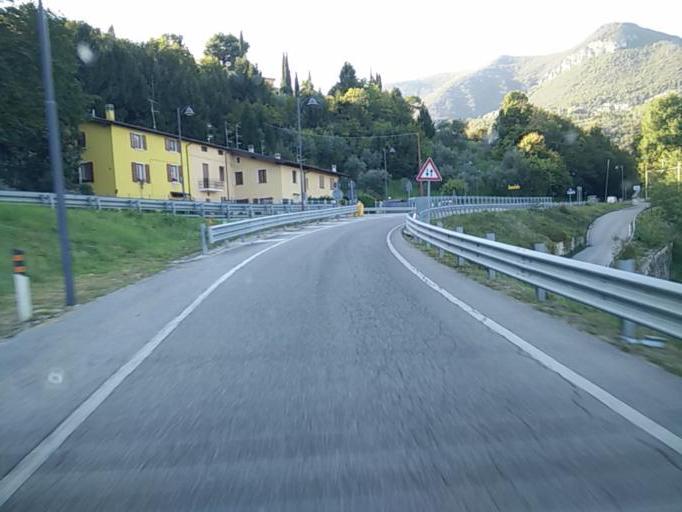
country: IT
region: Lombardy
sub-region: Provincia di Brescia
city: Roe Volciano
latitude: 45.6065
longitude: 10.4842
